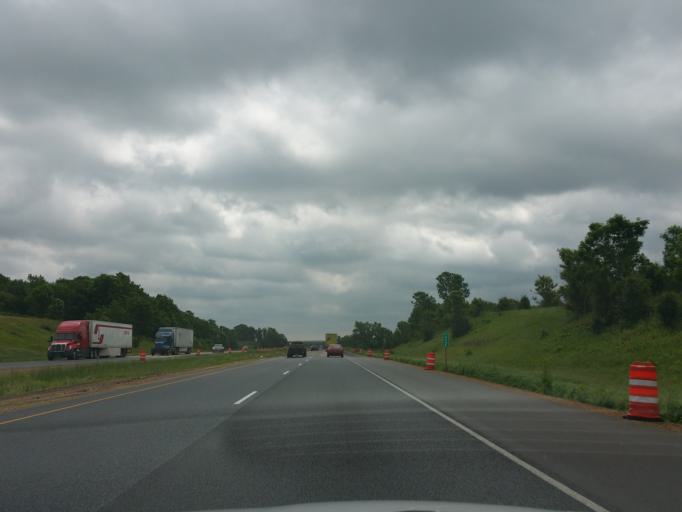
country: US
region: Wisconsin
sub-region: Saint Croix County
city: Woodville
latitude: 44.9374
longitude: -92.3292
